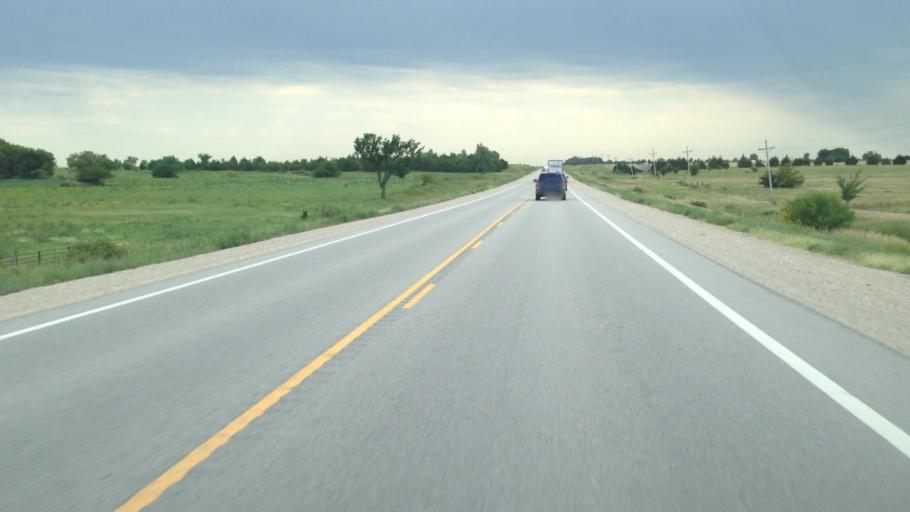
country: US
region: Kansas
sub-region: Coffey County
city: Burlington
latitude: 38.3297
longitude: -95.7290
